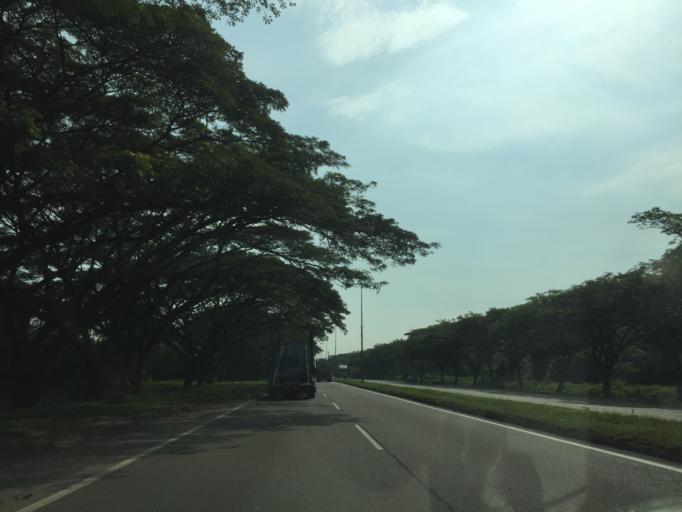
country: MY
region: Selangor
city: Klang
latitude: 2.9837
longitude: 101.4340
